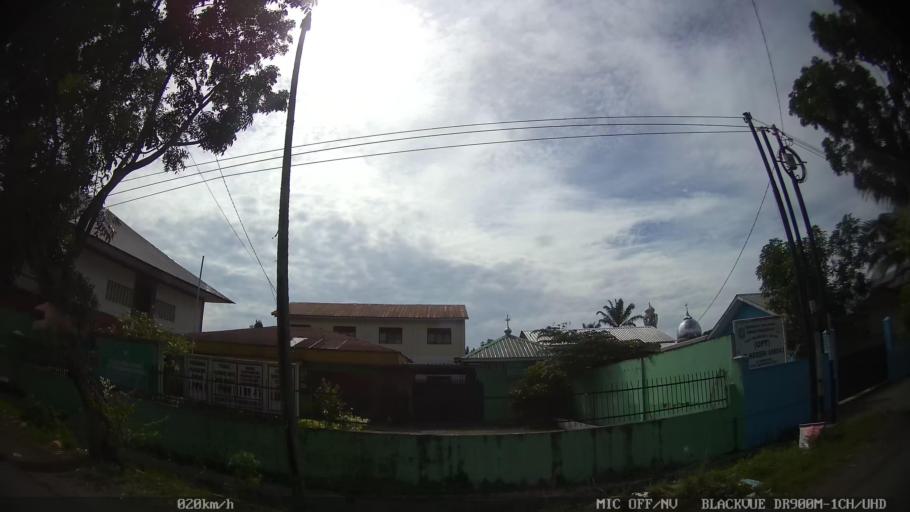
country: ID
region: North Sumatra
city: Sunggal
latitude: 3.6129
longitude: 98.6298
